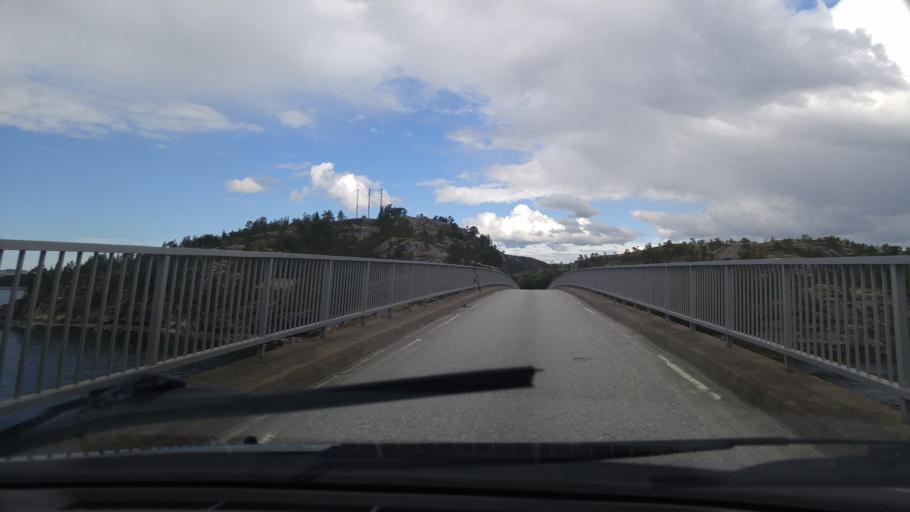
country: NO
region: Nord-Trondelag
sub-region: Naeroy
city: Kolvereid
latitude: 64.7494
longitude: 11.5671
